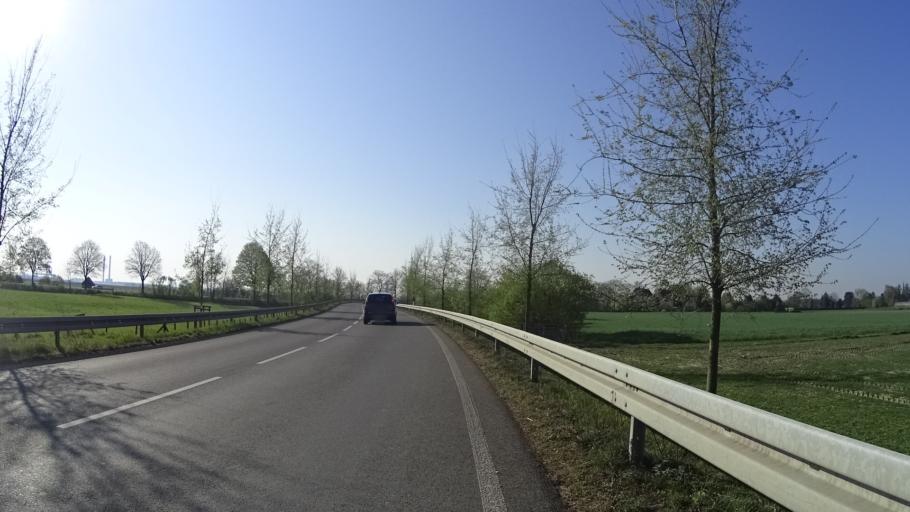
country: DE
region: North Rhine-Westphalia
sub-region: Regierungsbezirk Dusseldorf
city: Wesel
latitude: 51.6373
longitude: 6.5884
